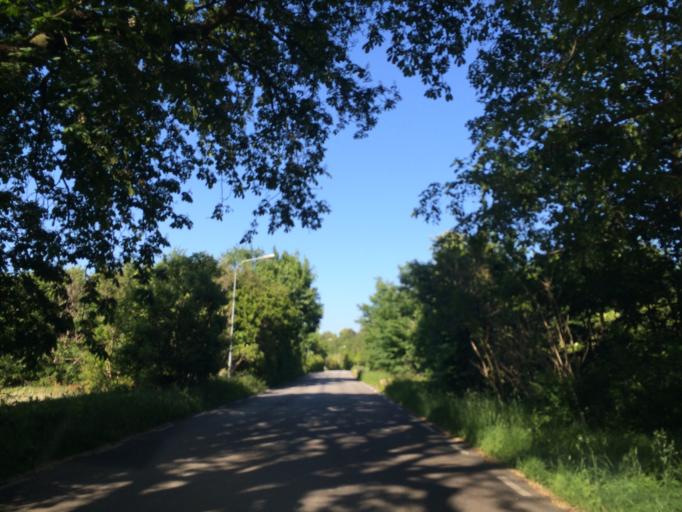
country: SE
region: Skane
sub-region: Lomma Kommun
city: Lomma
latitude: 55.6825
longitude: 13.0712
